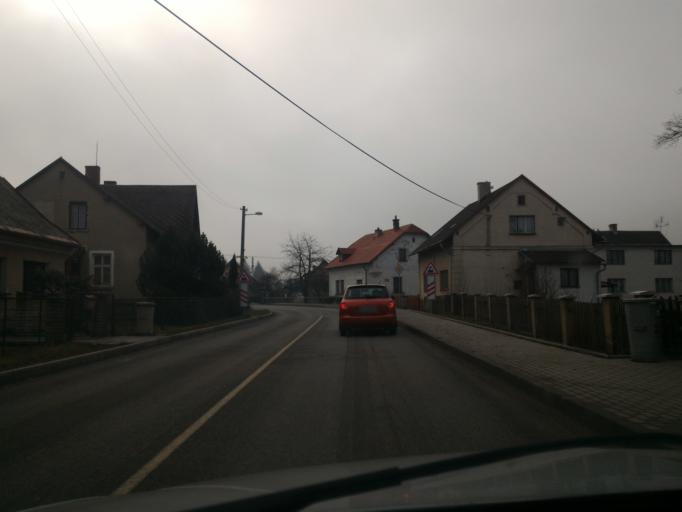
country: CZ
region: Liberecky
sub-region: Okres Liberec
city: Raspenava
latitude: 50.8952
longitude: 15.1458
